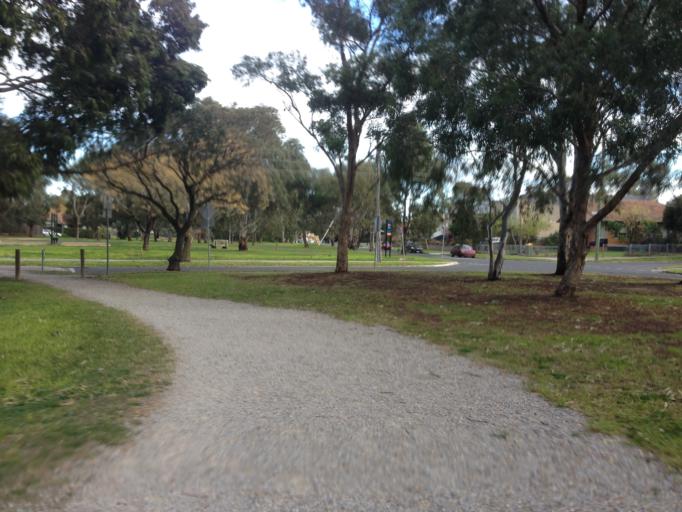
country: AU
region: Victoria
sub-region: Banyule
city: Bellfield
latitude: -37.7581
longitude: 145.0413
